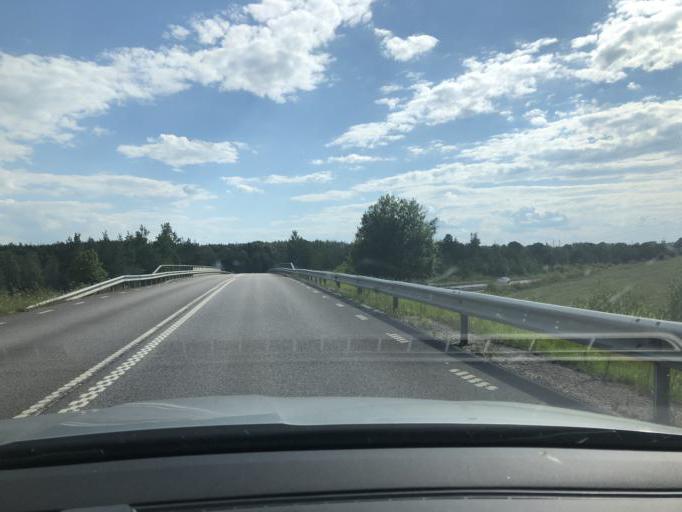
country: SE
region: OEstergoetland
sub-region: Mjolby Kommun
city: Mjolby
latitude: 58.3431
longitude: 15.1718
